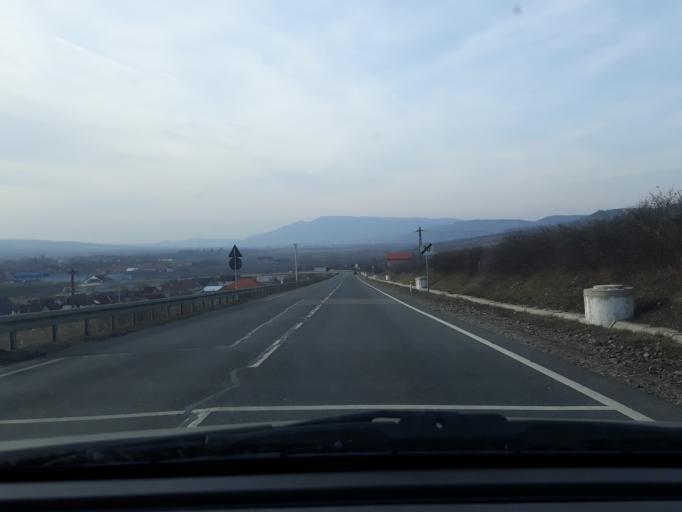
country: RO
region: Salaj
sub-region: Comuna Varsolt
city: Varsolt
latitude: 47.2111
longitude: 22.9296
